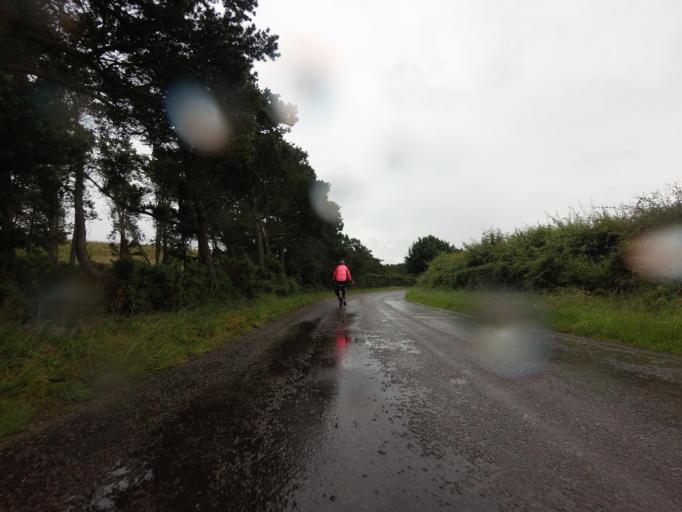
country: GB
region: Scotland
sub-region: Moray
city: Fochabers
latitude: 57.6645
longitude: -3.0736
